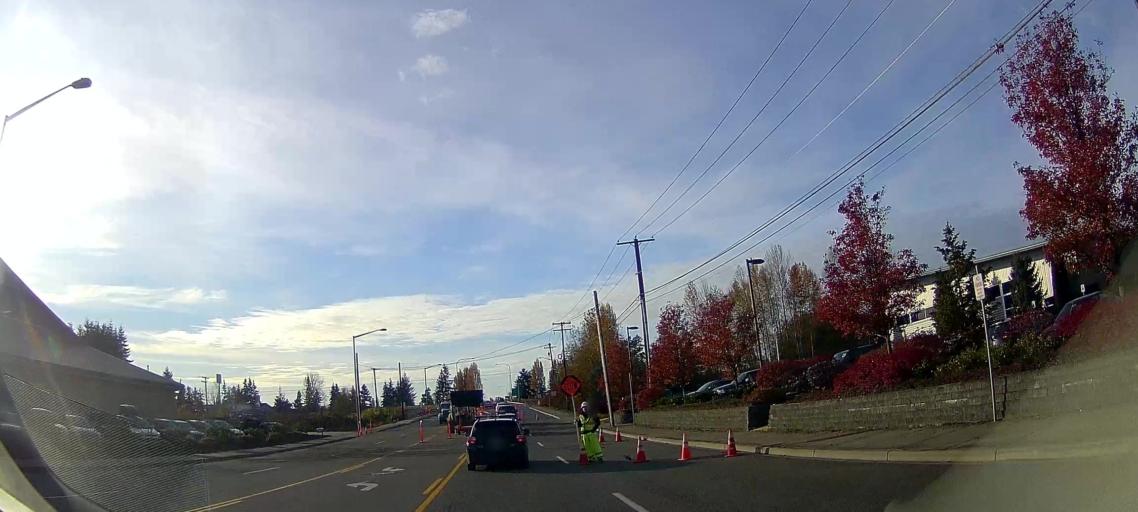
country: US
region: Washington
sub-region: Skagit County
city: Mount Vernon
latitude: 48.3995
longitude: -122.3260
